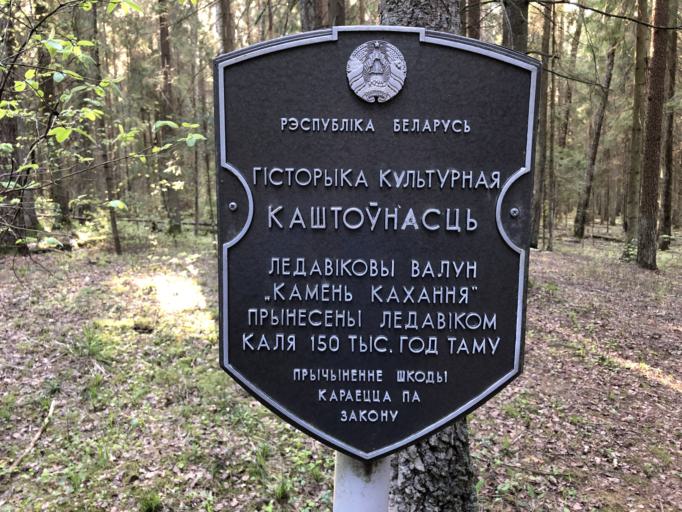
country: BY
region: Minsk
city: Zaslawye
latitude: 53.9533
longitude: 27.2656
